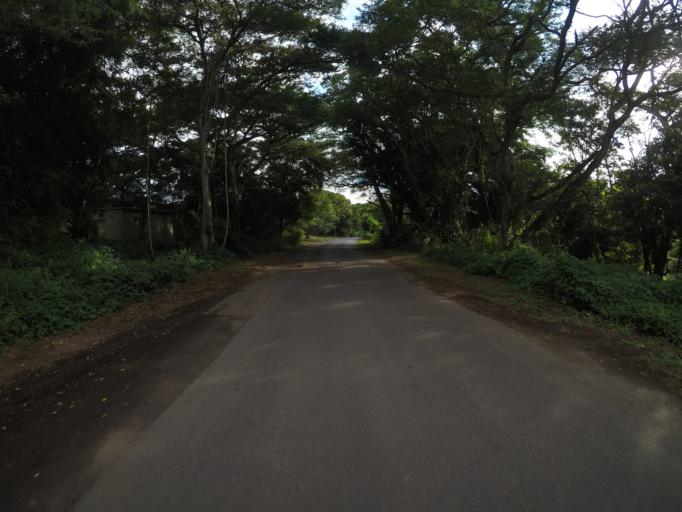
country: ZA
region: KwaZulu-Natal
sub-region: uMkhanyakude District Municipality
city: Mtubatuba
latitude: -28.3839
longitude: 32.4111
